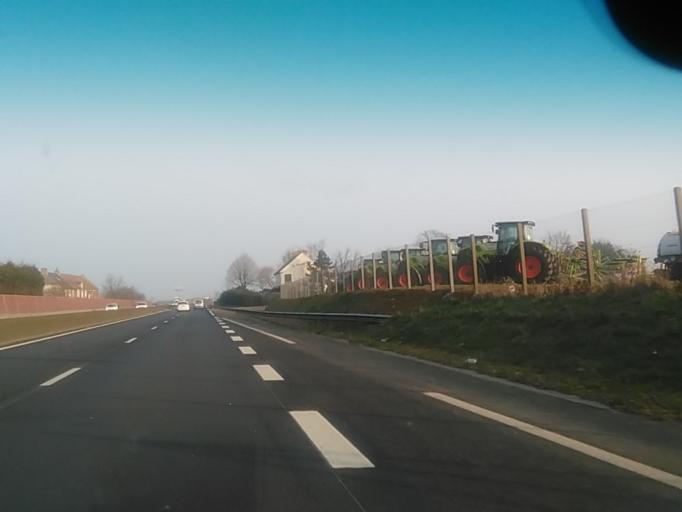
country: FR
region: Lower Normandy
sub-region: Departement du Calvados
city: Bourguebus
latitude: 49.0906
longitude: -0.3071
